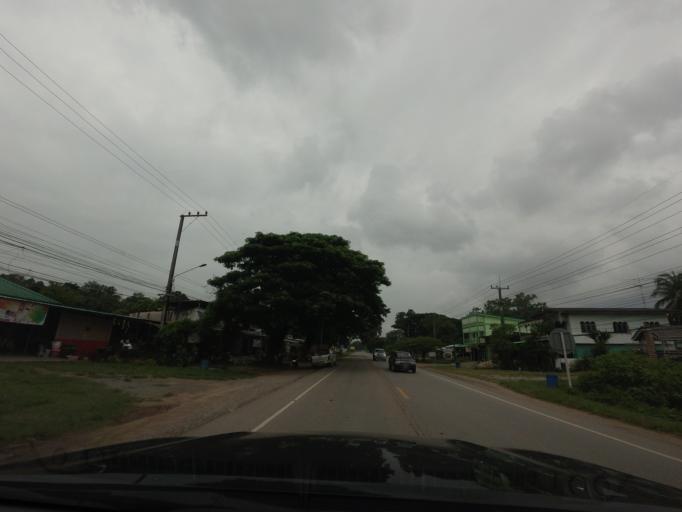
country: TH
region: Nong Khai
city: Si Chiang Mai
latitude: 17.9580
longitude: 102.5614
